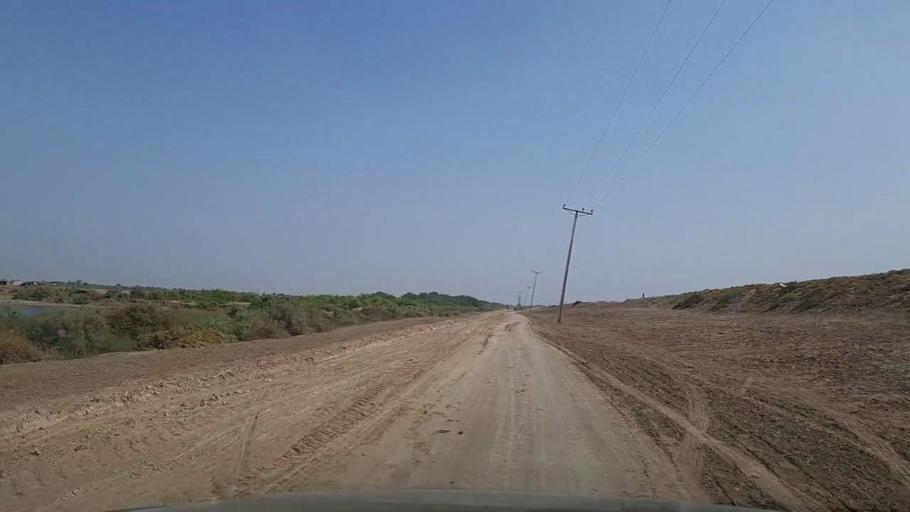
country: PK
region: Sindh
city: Thatta
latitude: 24.5907
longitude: 67.9391
